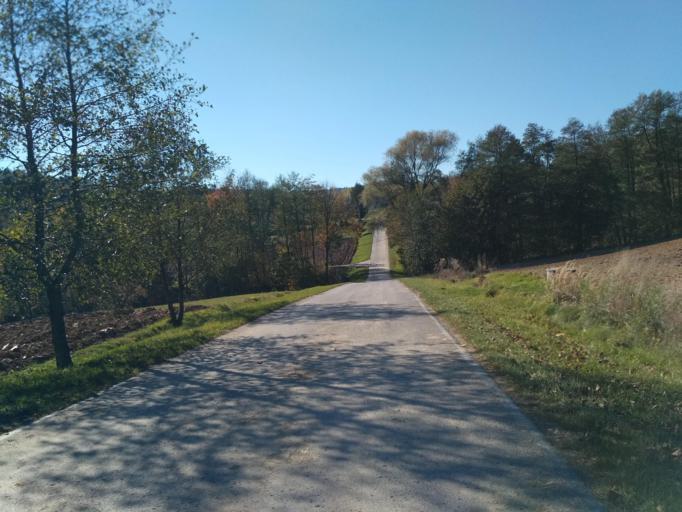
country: PL
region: Subcarpathian Voivodeship
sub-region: Powiat ropczycko-sedziszowski
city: Iwierzyce
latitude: 49.9753
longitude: 21.7235
